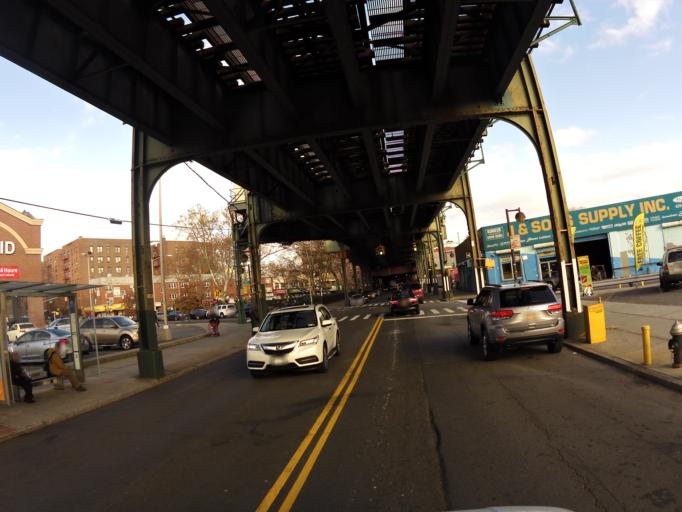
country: US
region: New York
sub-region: Queens County
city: Long Island City
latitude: 40.7436
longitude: -73.9143
